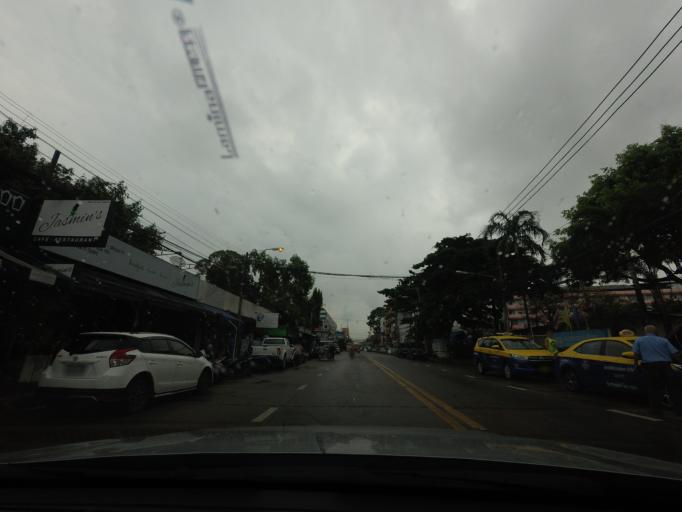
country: TH
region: Chon Buri
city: Phatthaya
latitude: 12.9372
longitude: 100.8850
